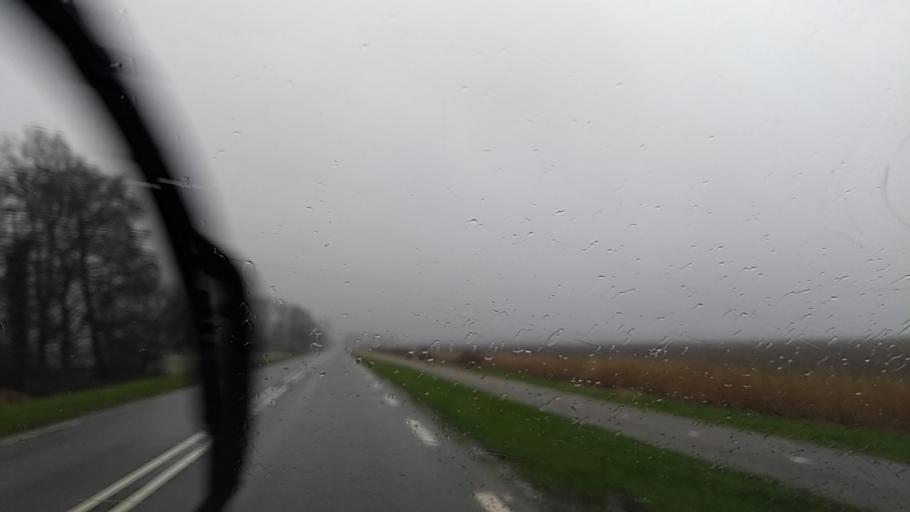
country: NL
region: Overijssel
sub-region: Gemeente Steenwijkerland
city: Blokzijl
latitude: 52.7332
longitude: 5.8605
